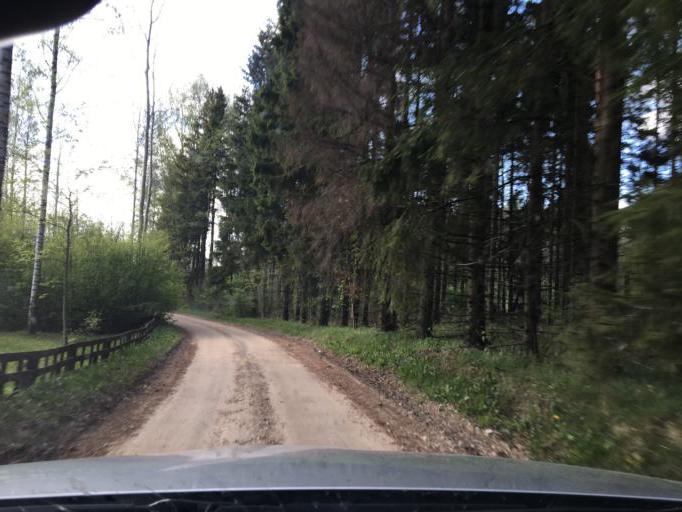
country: LV
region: Ozolnieku
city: Ozolnieki
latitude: 56.6706
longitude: 23.8751
